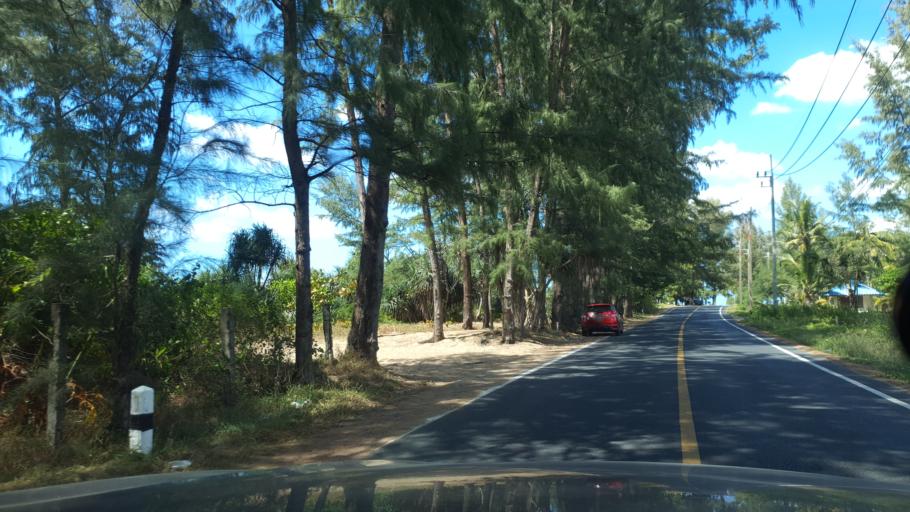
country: TH
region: Phangnga
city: Thai Mueang
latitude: 8.2942
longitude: 98.2727
